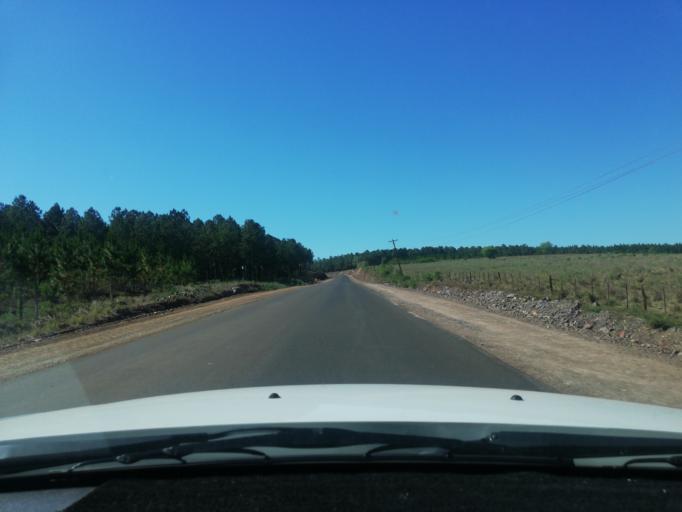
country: AR
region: Misiones
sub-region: Departamento de Candelaria
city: Candelaria
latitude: -27.5071
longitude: -55.7365
